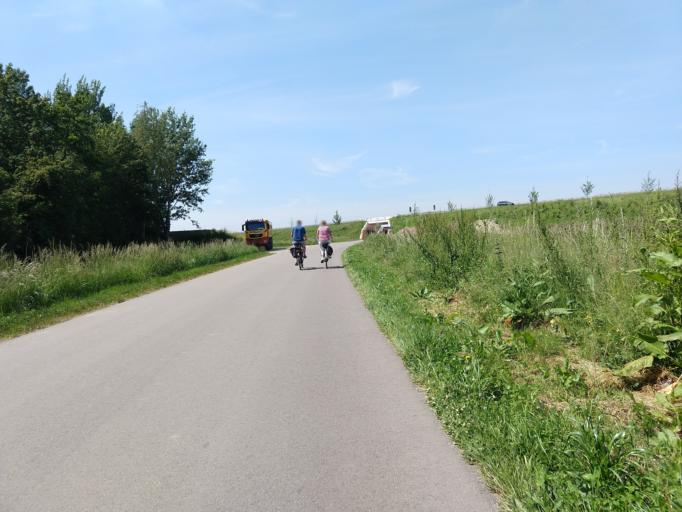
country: NL
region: Zeeland
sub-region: Gemeente Borsele
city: Borssele
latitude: 51.4851
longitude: 3.7955
